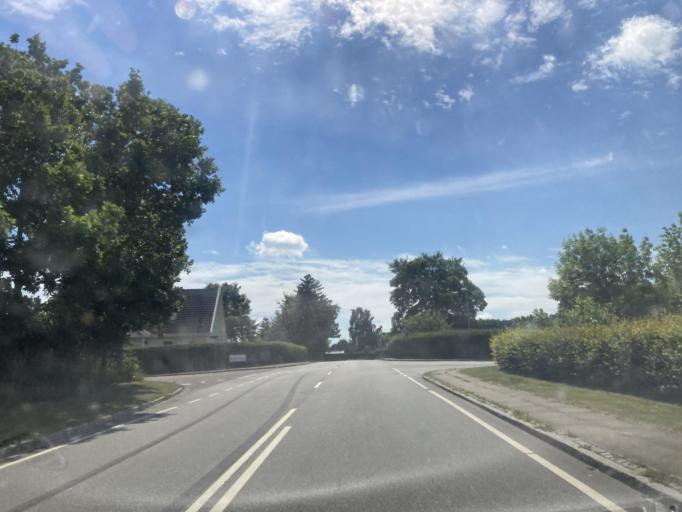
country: DK
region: Zealand
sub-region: Koge Kommune
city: Bjaeverskov
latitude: 55.4616
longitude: 12.0269
